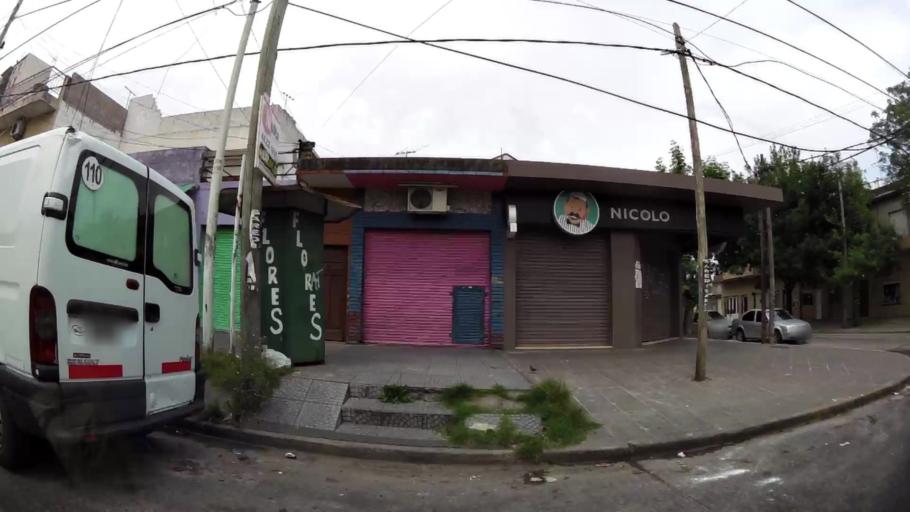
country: AR
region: Buenos Aires F.D.
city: Villa Lugano
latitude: -34.7058
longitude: -58.5042
